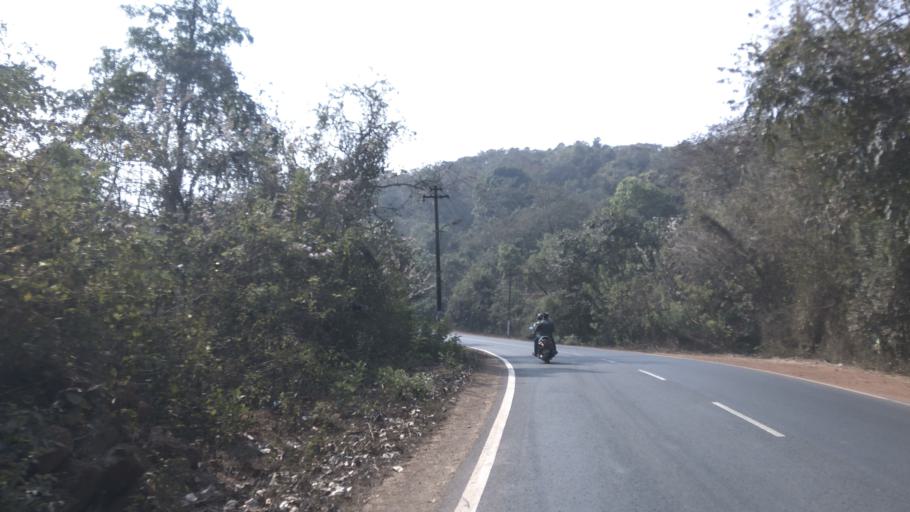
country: IN
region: Goa
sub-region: North Goa
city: Bandora
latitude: 15.4289
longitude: 73.9852
